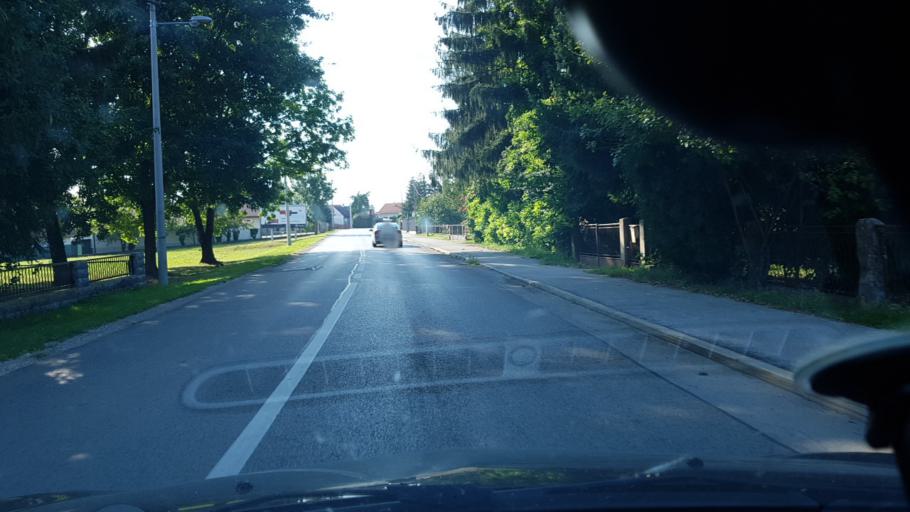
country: HR
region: Zagrebacka
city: Brdovec
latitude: 45.8685
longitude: 15.7568
